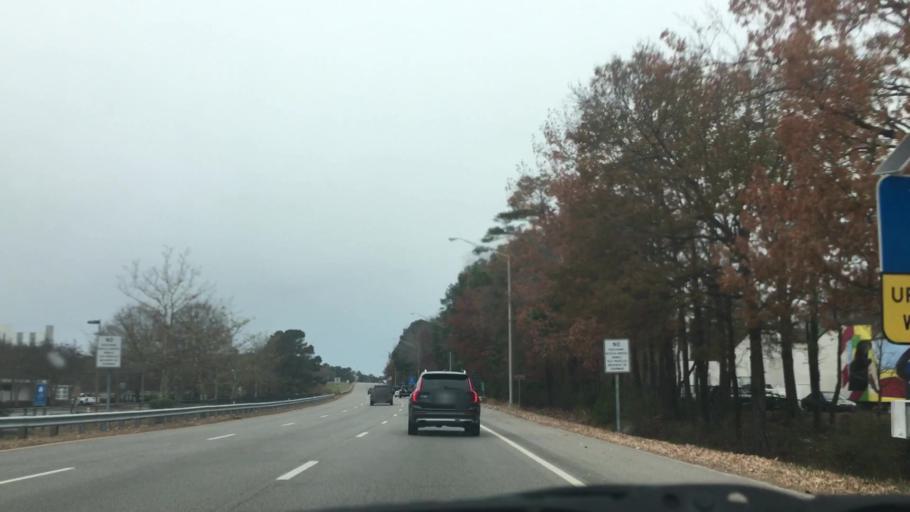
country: US
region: Virginia
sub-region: City of Virginia Beach
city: Virginia Beach
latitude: 36.8483
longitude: -75.9866
